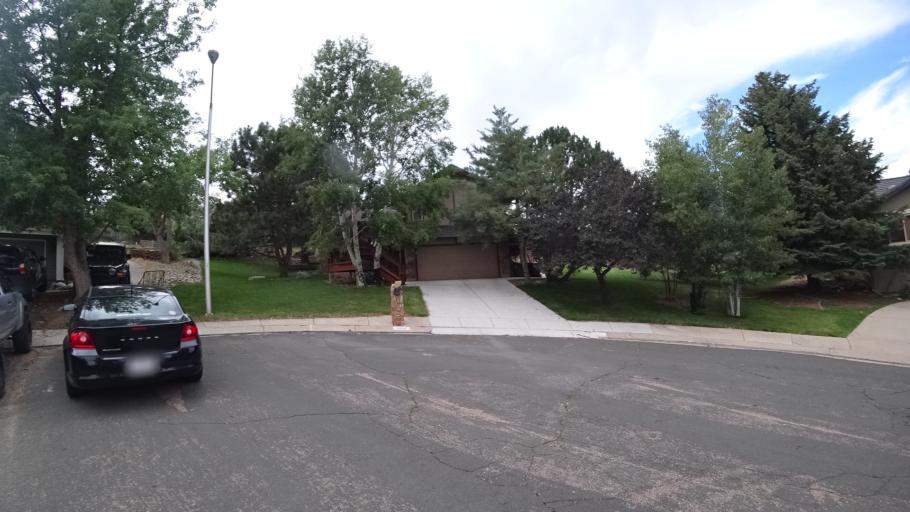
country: US
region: Colorado
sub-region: El Paso County
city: Colorado Springs
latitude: 38.9061
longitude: -104.8414
